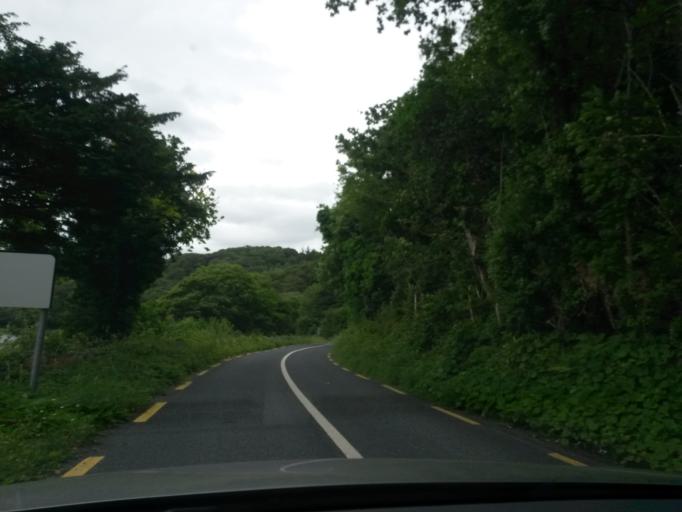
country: IE
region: Connaught
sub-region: County Leitrim
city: Manorhamilton
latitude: 54.2556
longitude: -8.3168
